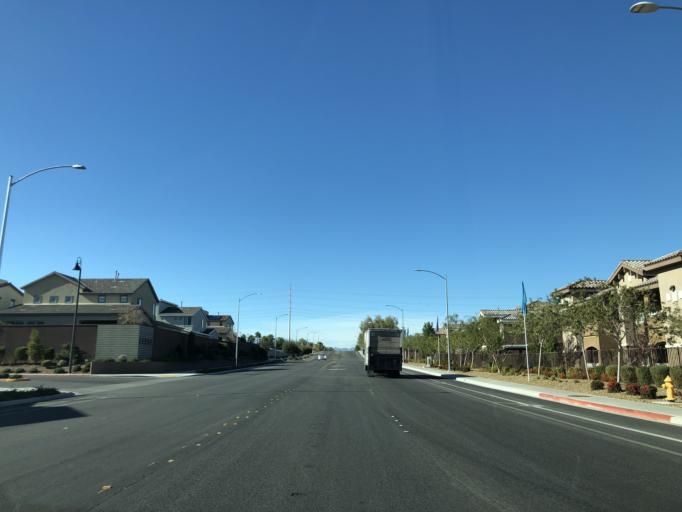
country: US
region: Nevada
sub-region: Clark County
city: Whitney
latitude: 36.0005
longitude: -115.0862
